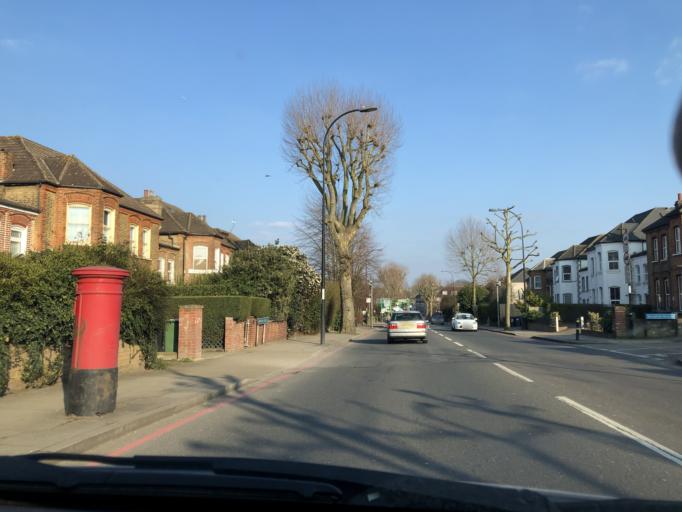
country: GB
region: England
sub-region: Greater London
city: Blackheath
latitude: 51.4452
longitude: 0.0008
